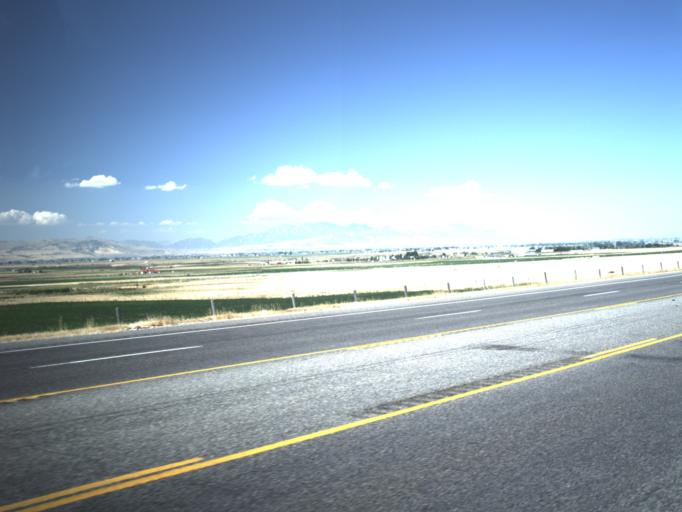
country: US
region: Utah
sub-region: Cache County
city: Richmond
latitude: 41.8941
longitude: -111.8148
